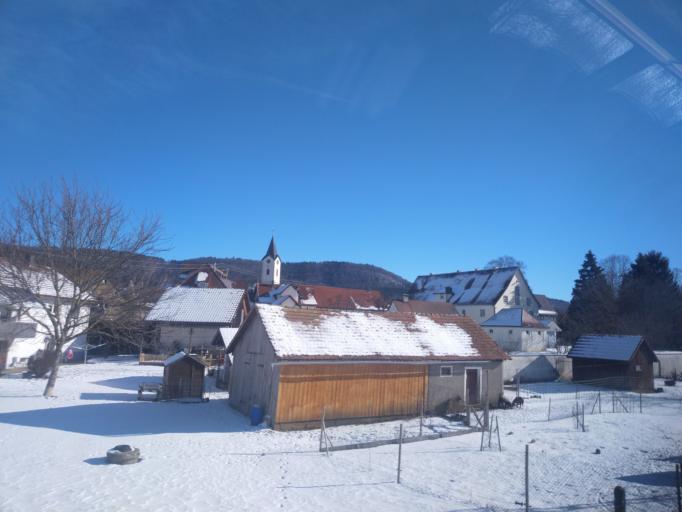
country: DE
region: Baden-Wuerttemberg
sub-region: Freiburg Region
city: Balgheim
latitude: 48.0656
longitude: 8.7607
